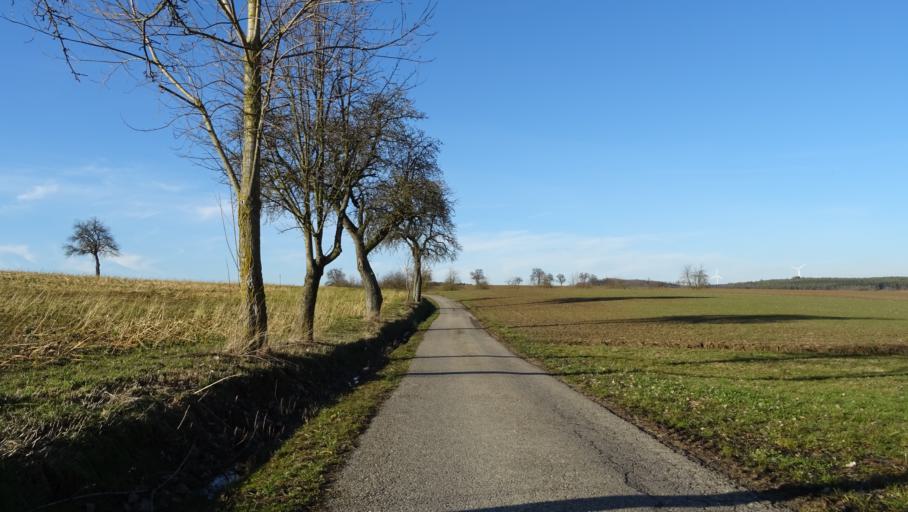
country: DE
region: Baden-Wuerttemberg
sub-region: Karlsruhe Region
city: Billigheim
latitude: 49.4173
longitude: 9.2645
